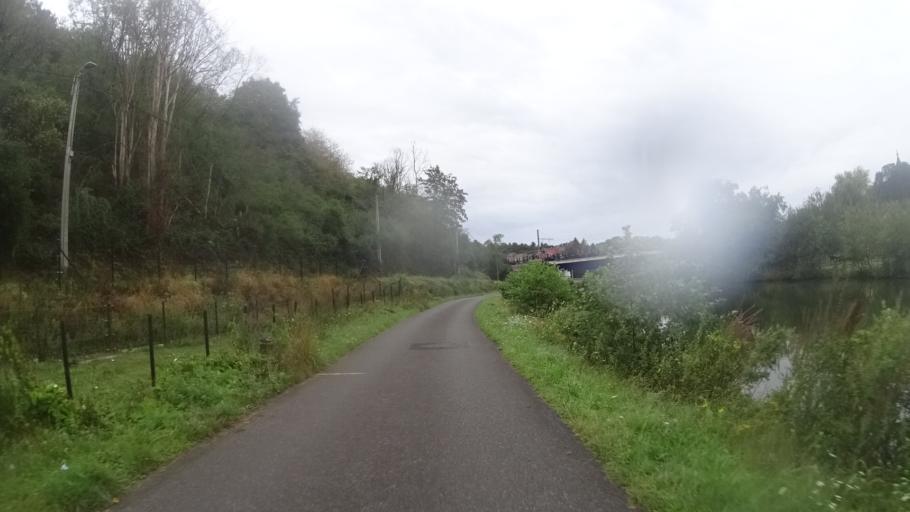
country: BE
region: Wallonia
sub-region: Province du Hainaut
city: Thuin
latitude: 50.3453
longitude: 4.2807
